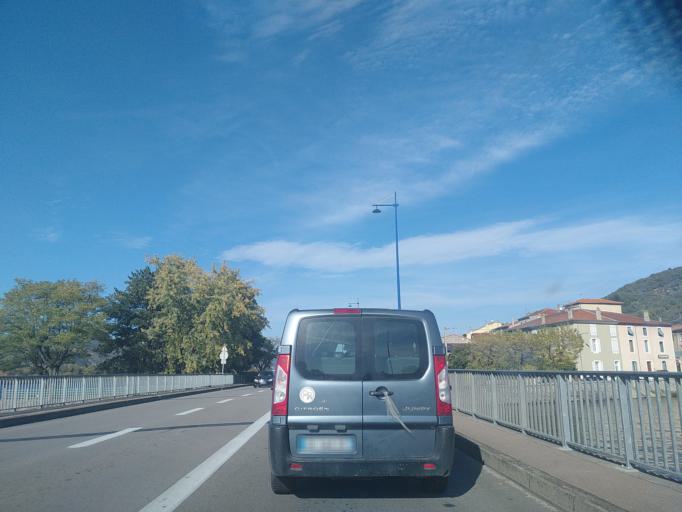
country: FR
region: Rhone-Alpes
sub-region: Departement de la Drome
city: Saint-Vallier
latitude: 45.1769
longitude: 4.8133
